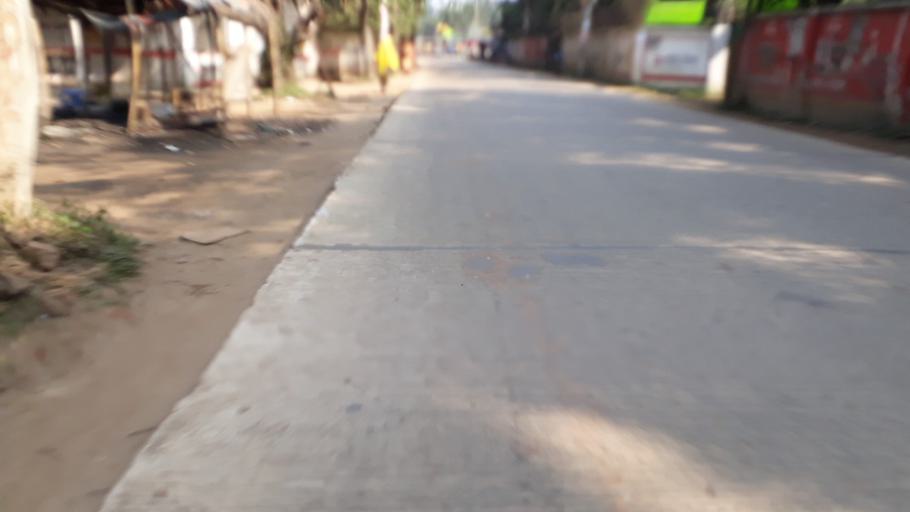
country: BD
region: Dhaka
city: Tungi
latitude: 23.8876
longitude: 90.3157
